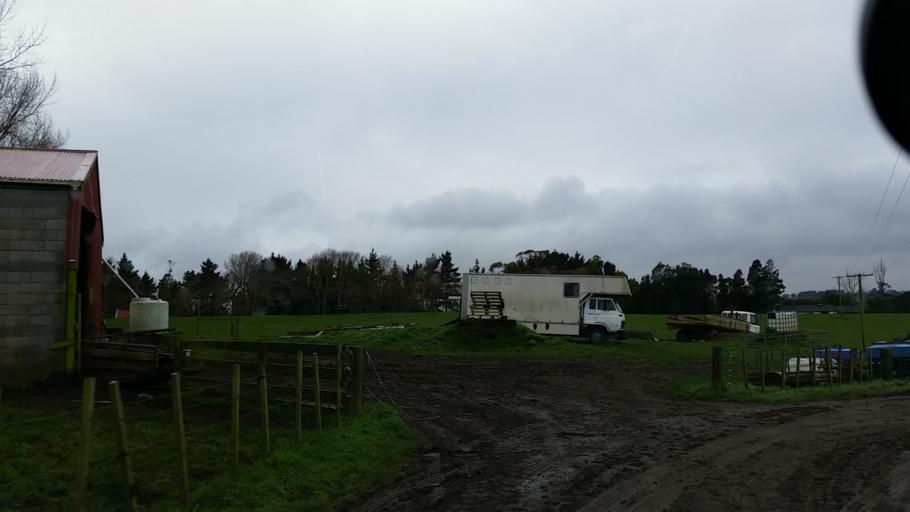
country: NZ
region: Taranaki
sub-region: South Taranaki District
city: Patea
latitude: -39.7696
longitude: 174.7106
